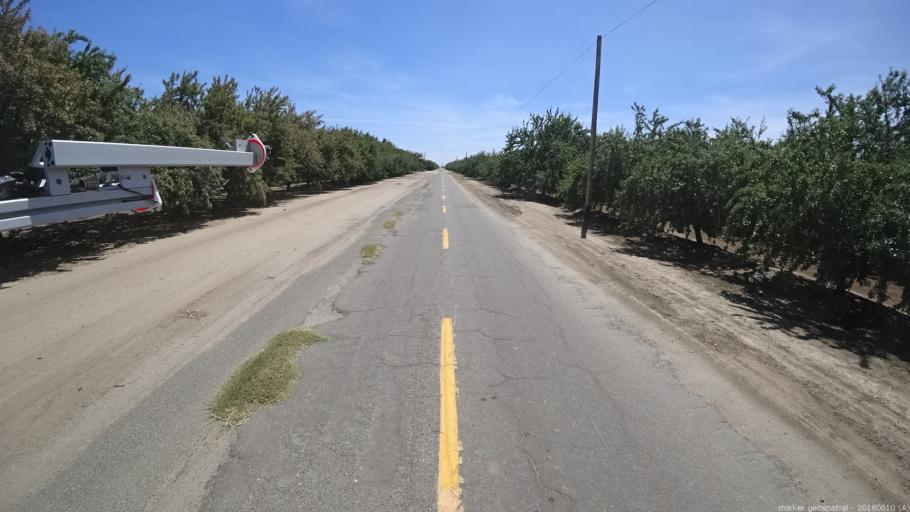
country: US
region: California
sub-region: Madera County
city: Chowchilla
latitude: 37.0398
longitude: -120.3986
